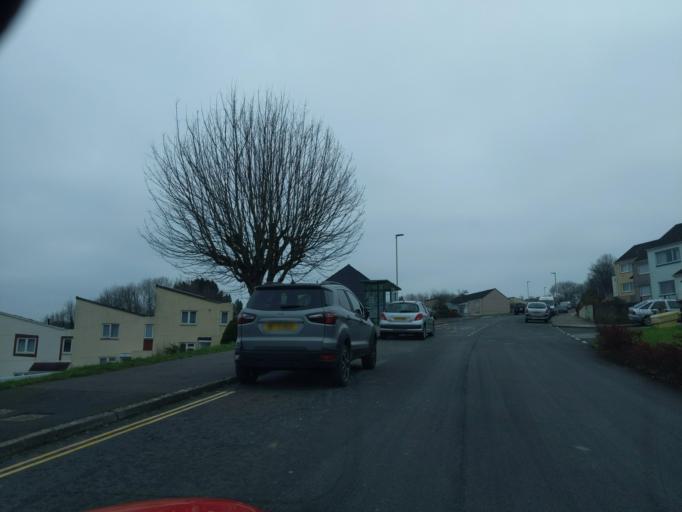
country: GB
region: England
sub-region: Plymouth
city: Plymstock
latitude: 50.3942
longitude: -4.1027
